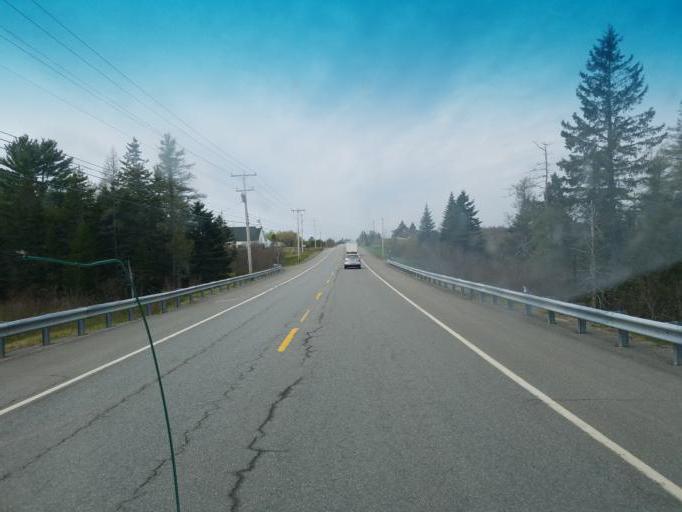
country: US
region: Maine
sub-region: Washington County
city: East Machias
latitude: 44.7575
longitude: -67.2280
